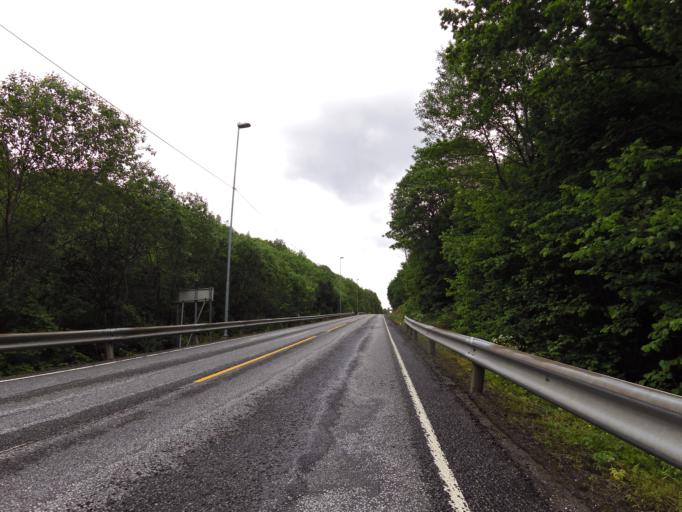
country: NO
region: Vest-Agder
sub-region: Farsund
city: Farsund
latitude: 58.1113
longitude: 6.9361
